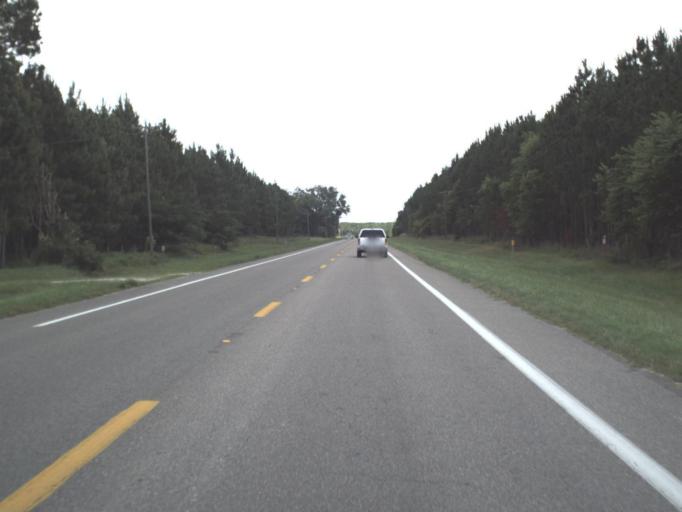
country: US
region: Florida
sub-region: Lafayette County
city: Mayo
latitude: 29.9589
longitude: -82.9663
